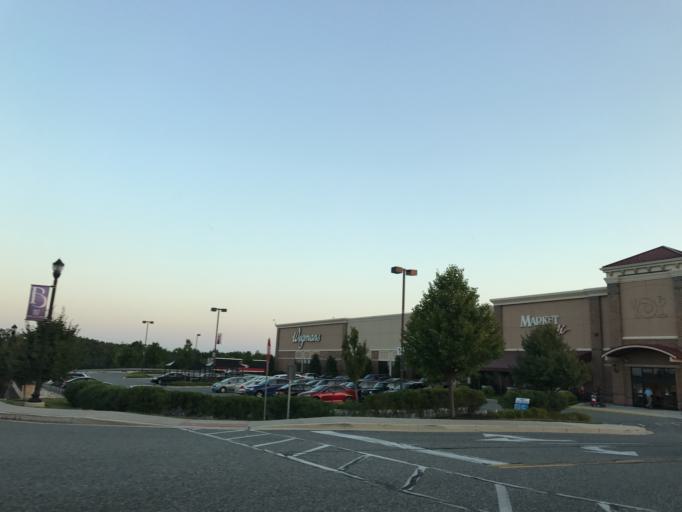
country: US
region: Maryland
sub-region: Harford County
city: Bel Air South
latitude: 39.4671
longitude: -76.3085
